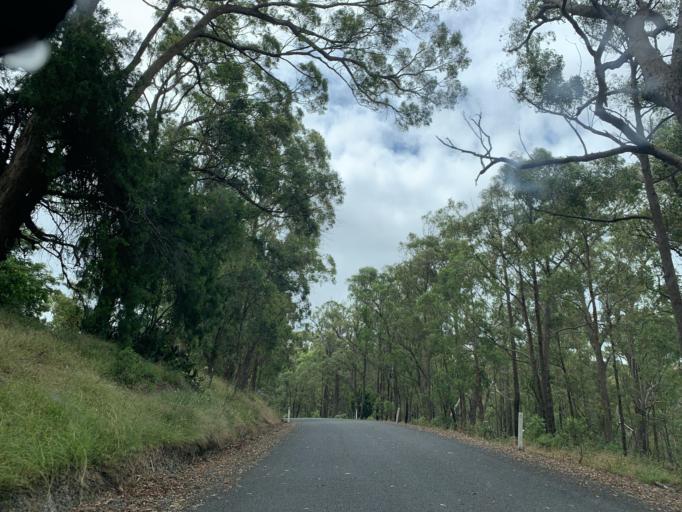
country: AU
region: Victoria
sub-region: Latrobe
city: Traralgon
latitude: -38.1063
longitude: 146.5365
